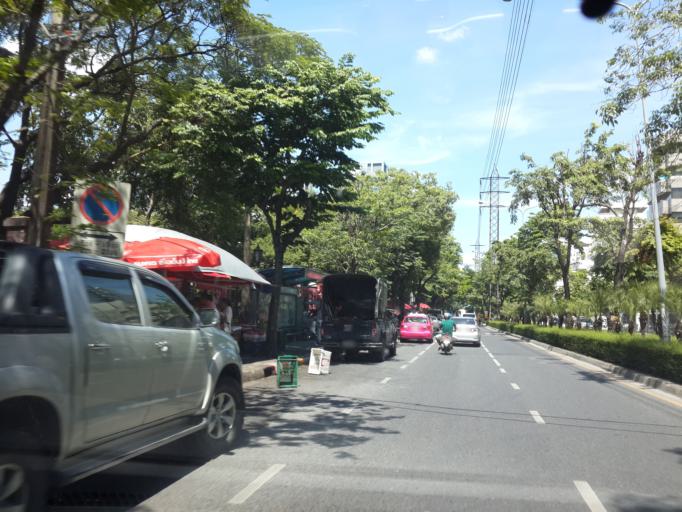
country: TH
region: Bangkok
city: Pathum Wan
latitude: 13.7342
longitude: 100.5411
